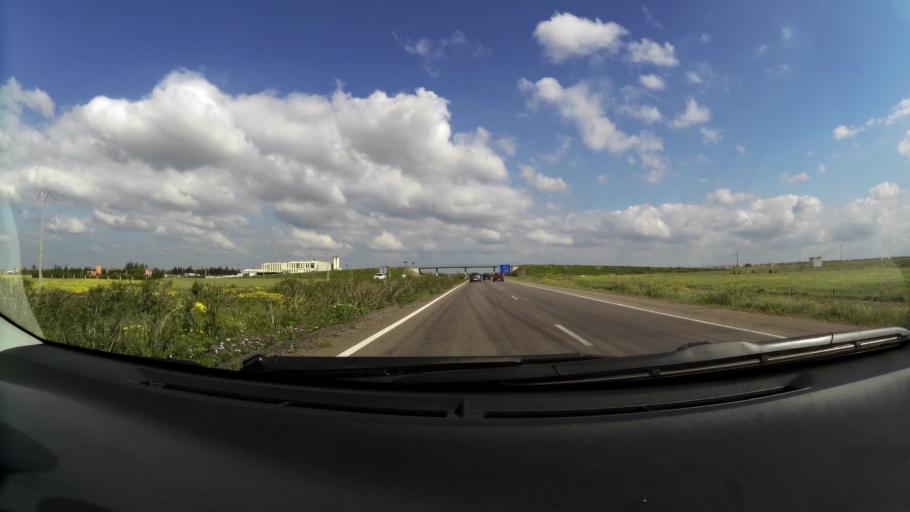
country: MA
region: Chaouia-Ouardigha
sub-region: Settat Province
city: Berrechid
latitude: 33.3135
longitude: -7.5969
